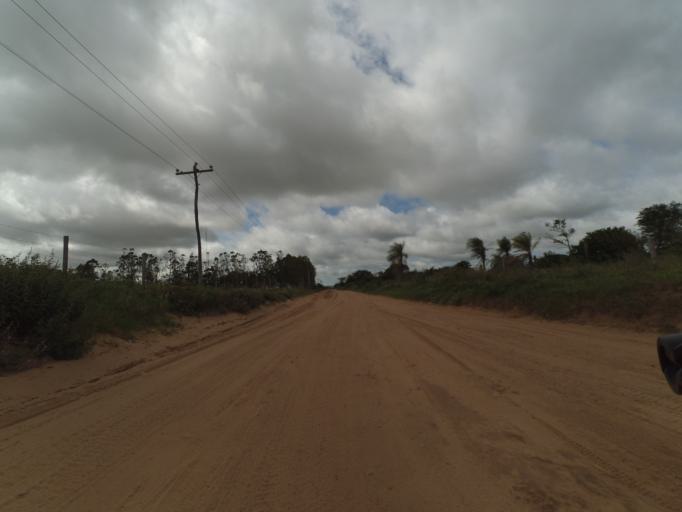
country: BO
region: Santa Cruz
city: Santa Cruz de la Sierra
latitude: -17.8956
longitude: -63.2415
